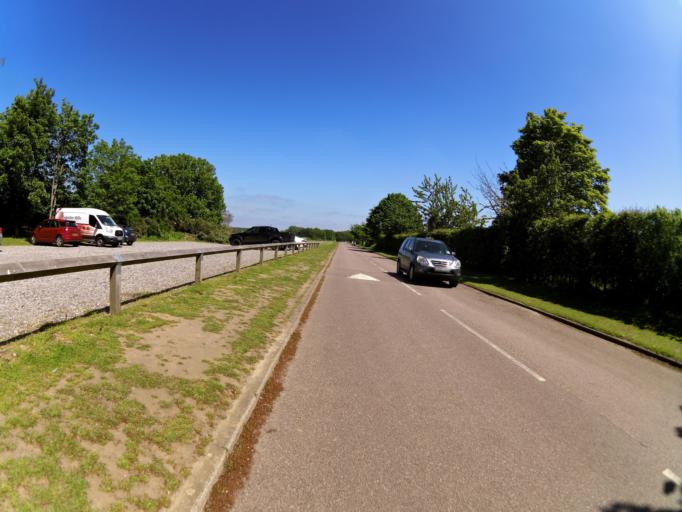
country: GB
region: England
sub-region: Essex
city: Mistley
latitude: 51.9750
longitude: 1.1403
